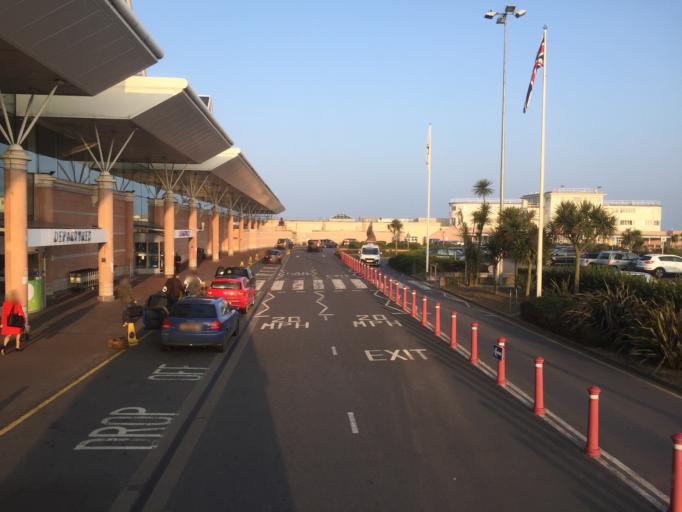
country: JE
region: St Helier
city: Saint Helier
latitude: 49.2052
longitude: -2.1937
